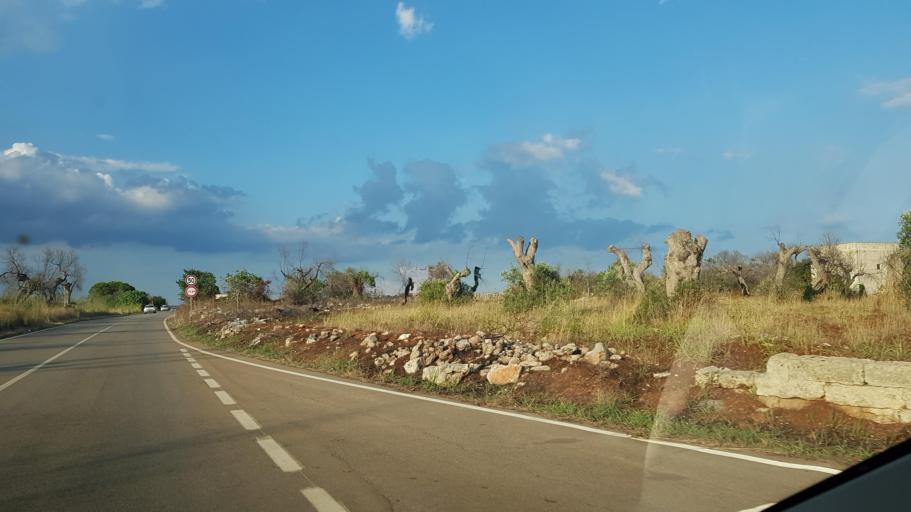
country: IT
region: Apulia
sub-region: Provincia di Lecce
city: Acquarica del Capo
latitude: 39.8869
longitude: 18.2394
